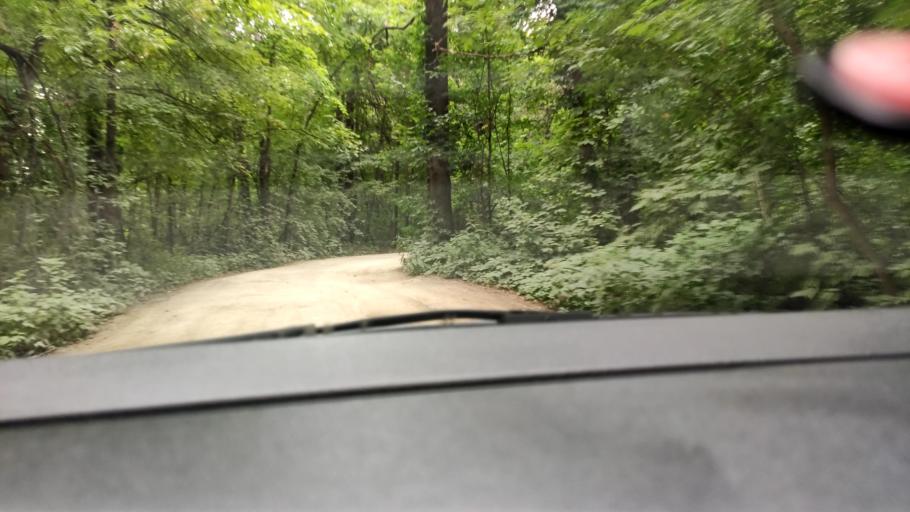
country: RU
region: Voronezj
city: Ramon'
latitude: 51.8898
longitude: 39.3520
